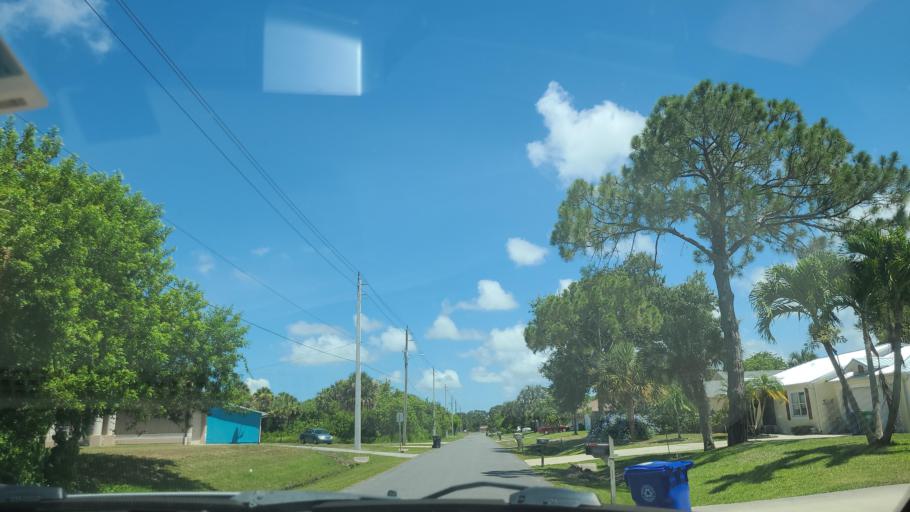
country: US
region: Florida
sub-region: Indian River County
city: Sebastian
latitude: 27.7829
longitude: -80.4832
